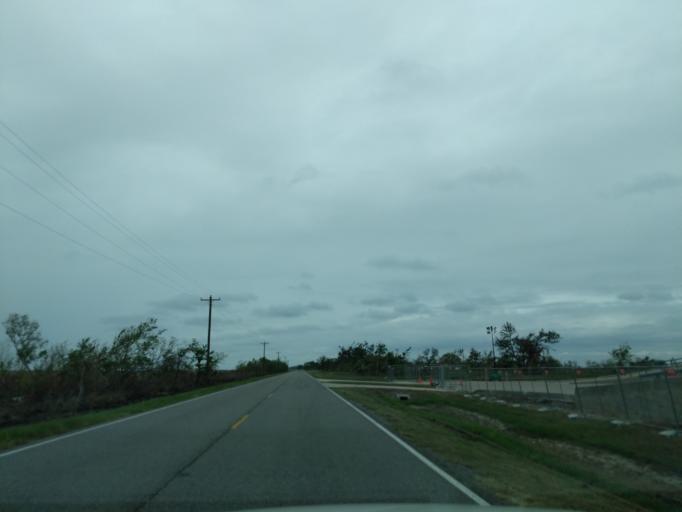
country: US
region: Louisiana
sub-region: Cameron Parish
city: Cameron
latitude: 29.7869
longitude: -93.1500
